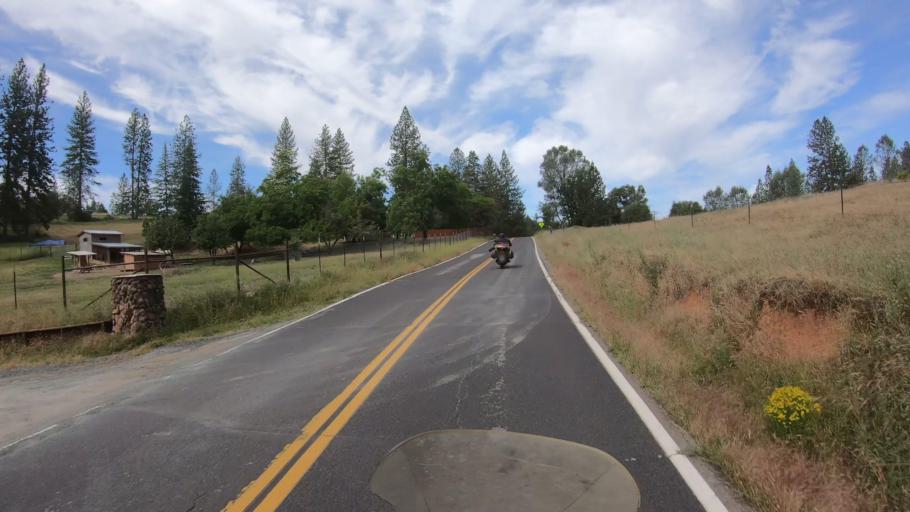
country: US
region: California
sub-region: Tuolumne County
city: Tuolumne City
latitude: 37.8504
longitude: -120.1528
